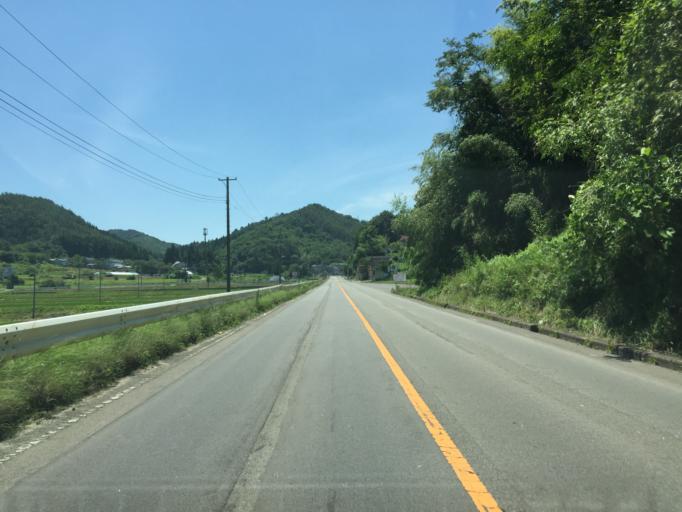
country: JP
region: Fukushima
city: Hobaramachi
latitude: 37.7517
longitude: 140.5367
